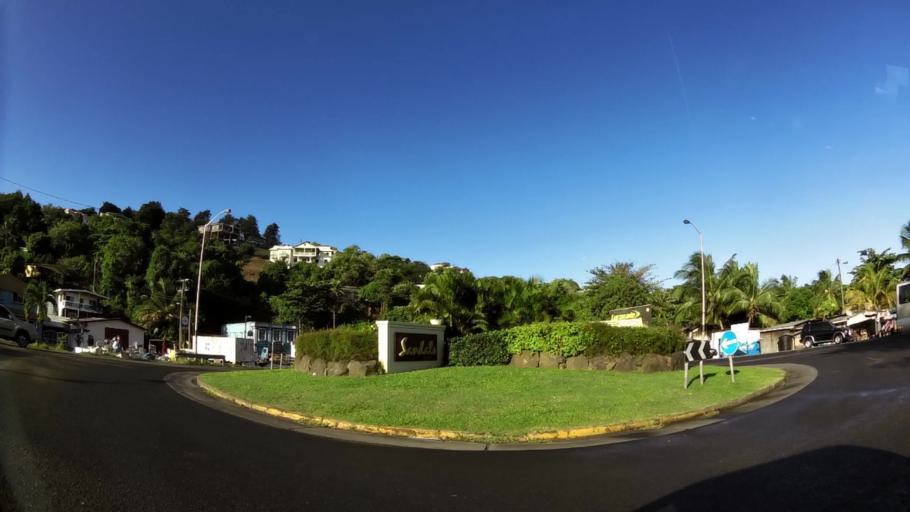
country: LC
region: Castries Quarter
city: Castries
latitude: 14.0106
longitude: -60.9999
